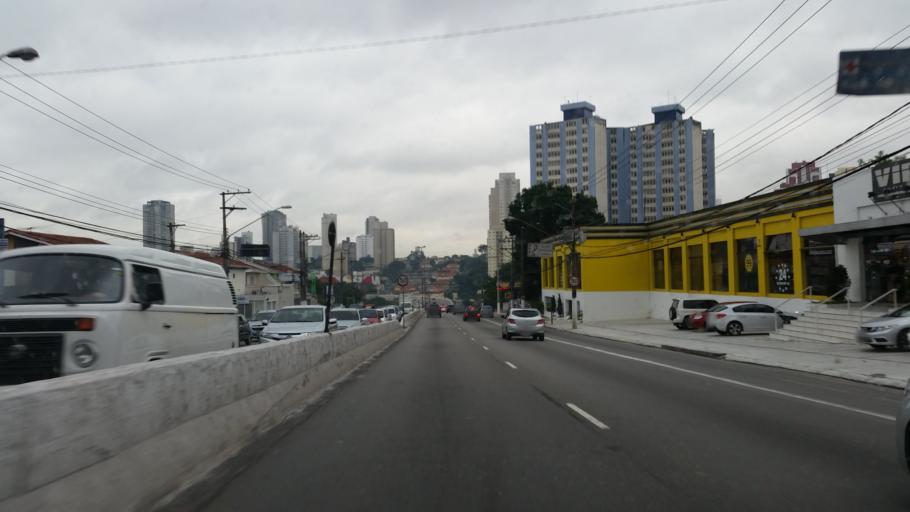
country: BR
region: Sao Paulo
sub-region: Diadema
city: Diadema
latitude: -23.6477
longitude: -46.6754
